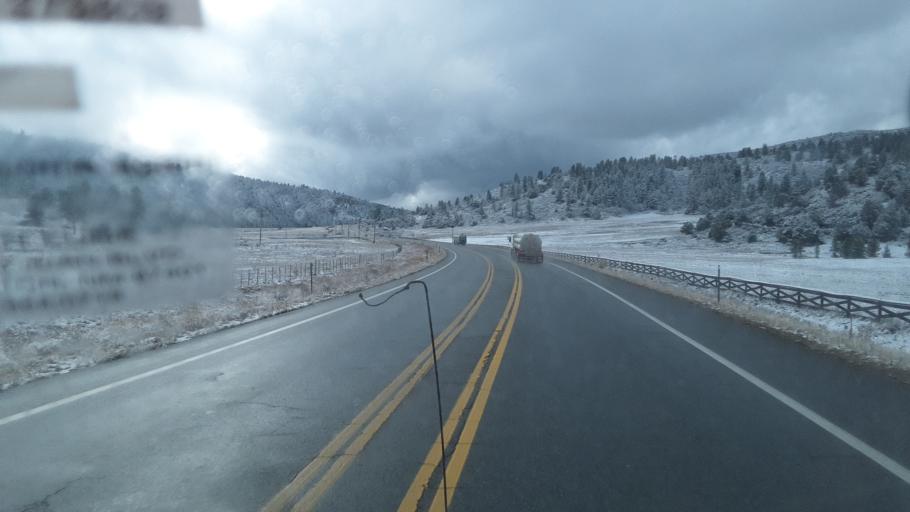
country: US
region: Colorado
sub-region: Archuleta County
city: Pagosa Springs
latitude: 37.2267
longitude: -107.2136
